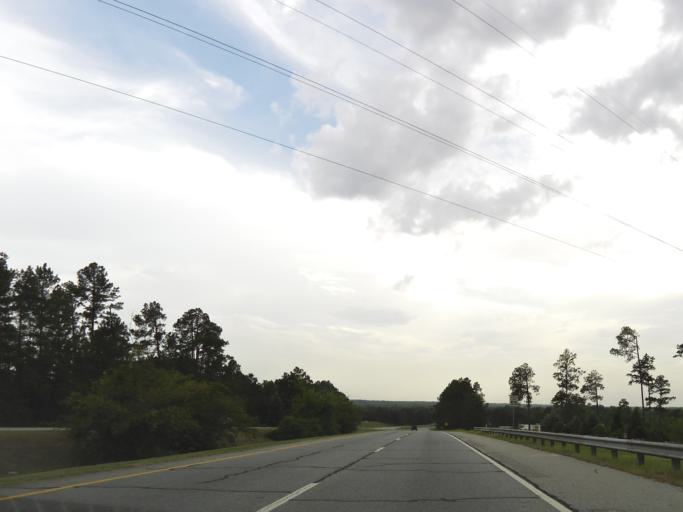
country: US
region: Georgia
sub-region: Bibb County
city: West Point
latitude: 32.8059
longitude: -83.7326
